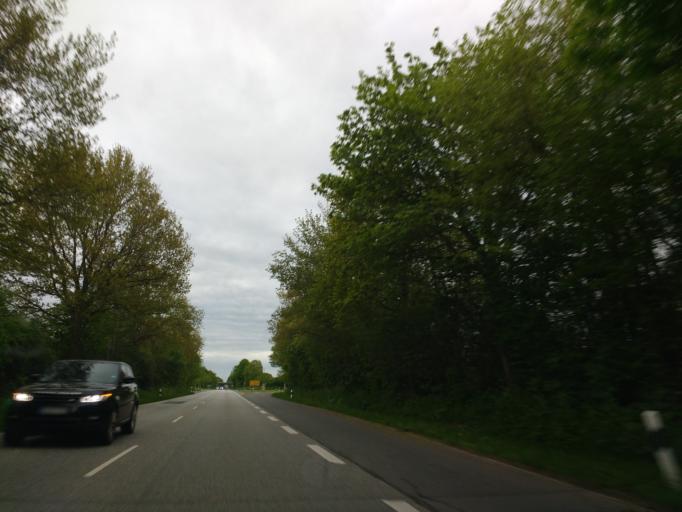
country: DE
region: Schleswig-Holstein
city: Dorphof
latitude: 54.6326
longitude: 9.9636
